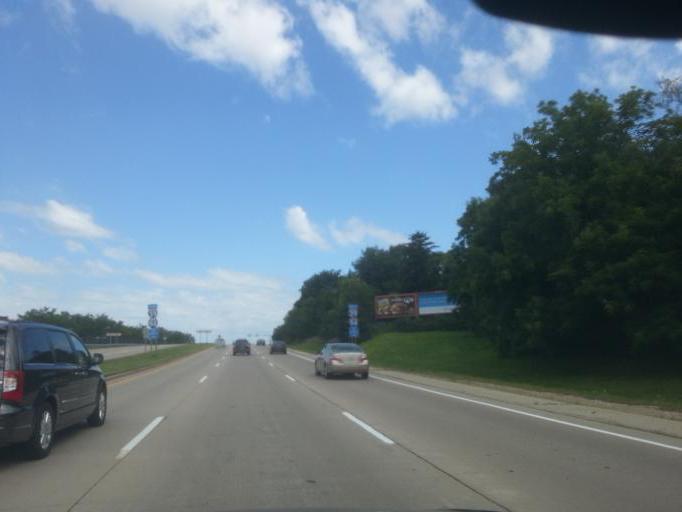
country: US
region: Wisconsin
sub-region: Dane County
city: Monona
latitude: 43.1120
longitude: -89.3194
